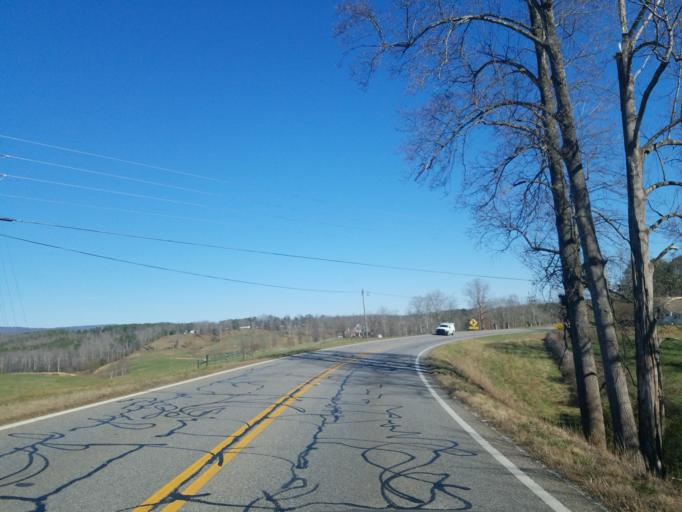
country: US
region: Georgia
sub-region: Pickens County
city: Nelson
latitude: 34.4133
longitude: -84.4157
